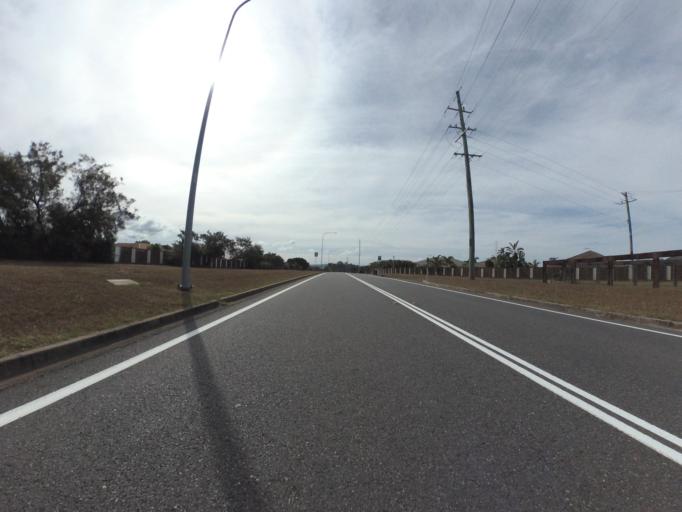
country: AU
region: Queensland
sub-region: Brisbane
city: Moggill
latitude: -27.5736
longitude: 152.8717
